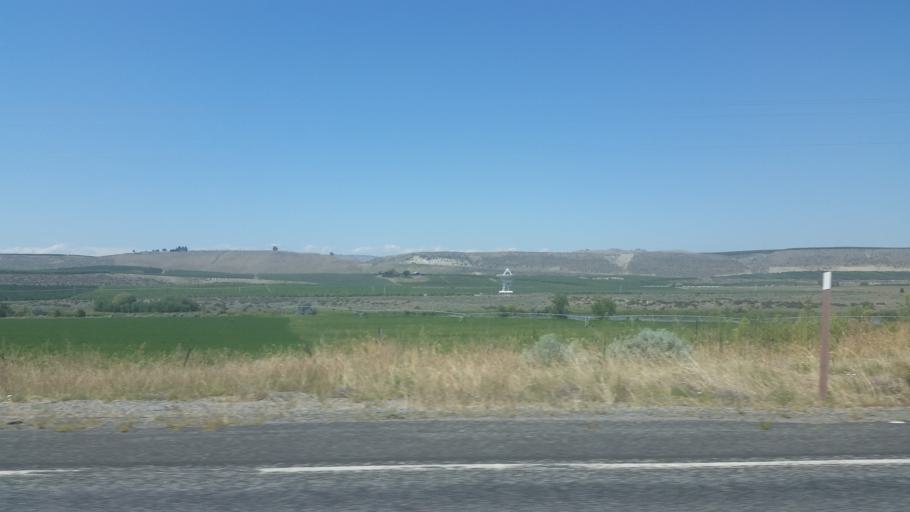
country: US
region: Washington
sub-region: Okanogan County
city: Brewster
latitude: 48.1285
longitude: -119.6727
